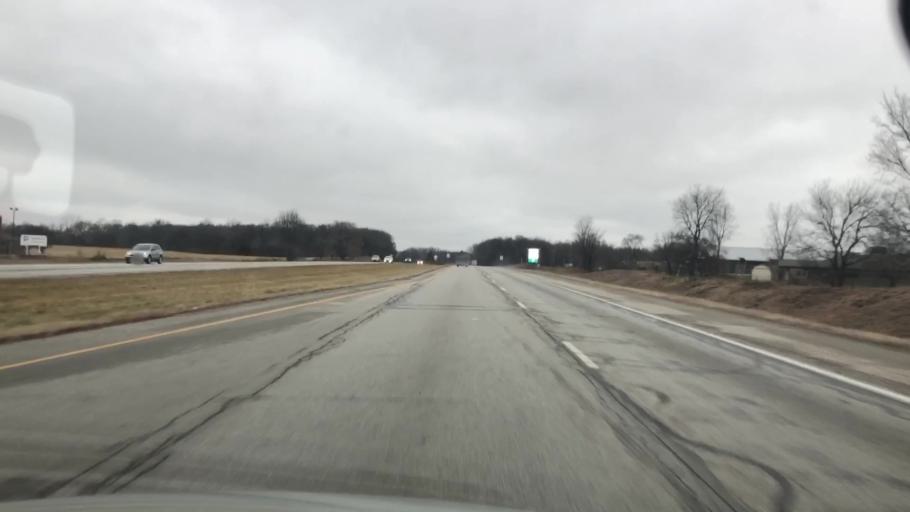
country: US
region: Indiana
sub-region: Kosciusko County
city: Winona Lake
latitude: 41.2535
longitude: -85.8289
